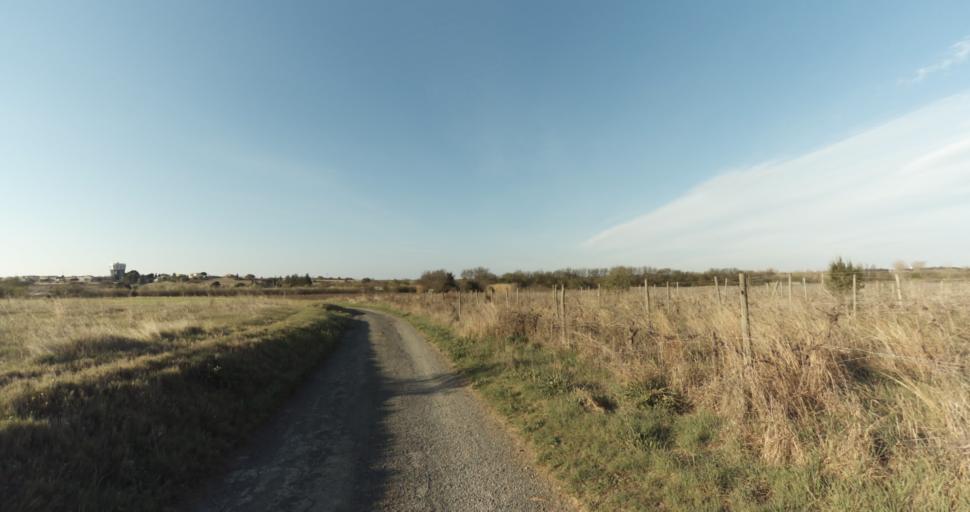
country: FR
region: Languedoc-Roussillon
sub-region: Departement de l'Herault
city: Marseillan
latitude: 43.3708
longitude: 3.5261
